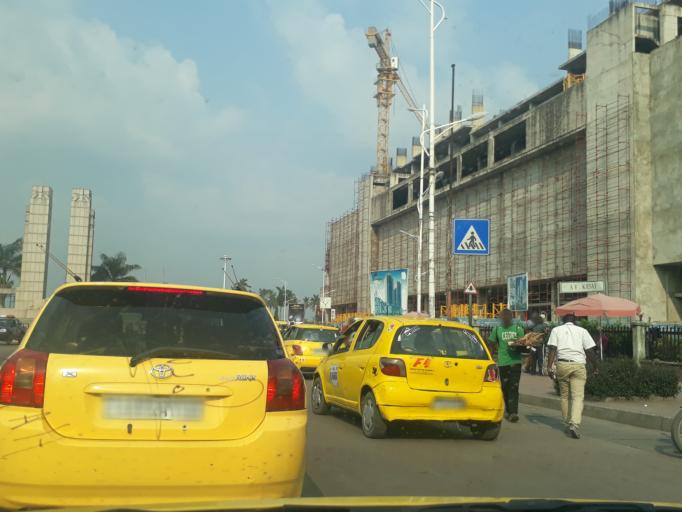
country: CD
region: Kinshasa
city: Kinshasa
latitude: -4.3019
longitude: 15.3156
